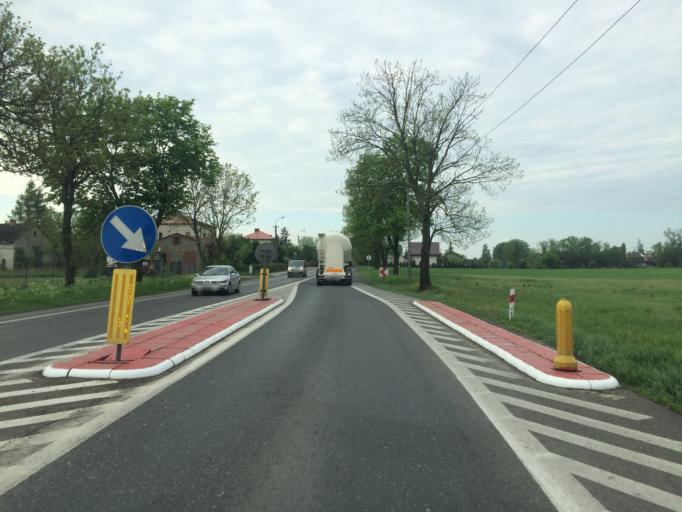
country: PL
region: Masovian Voivodeship
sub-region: Powiat mlawski
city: Wisniewo
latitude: 53.0705
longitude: 20.3497
